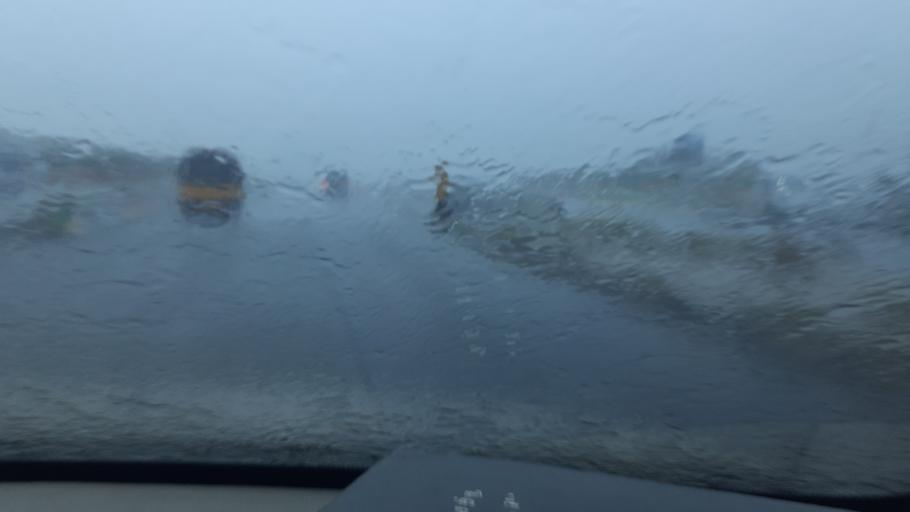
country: IN
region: Tamil Nadu
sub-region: Virudhunagar
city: Sattur
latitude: 9.4552
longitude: 77.9304
